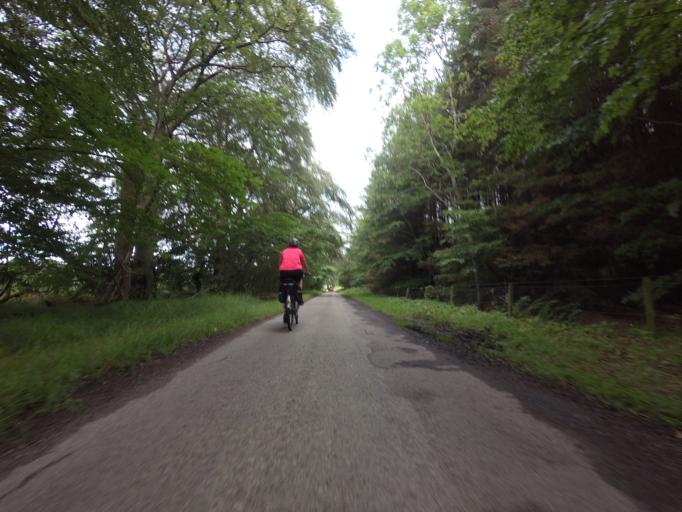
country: GB
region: Scotland
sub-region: Moray
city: Hopeman
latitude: 57.6713
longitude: -3.3987
